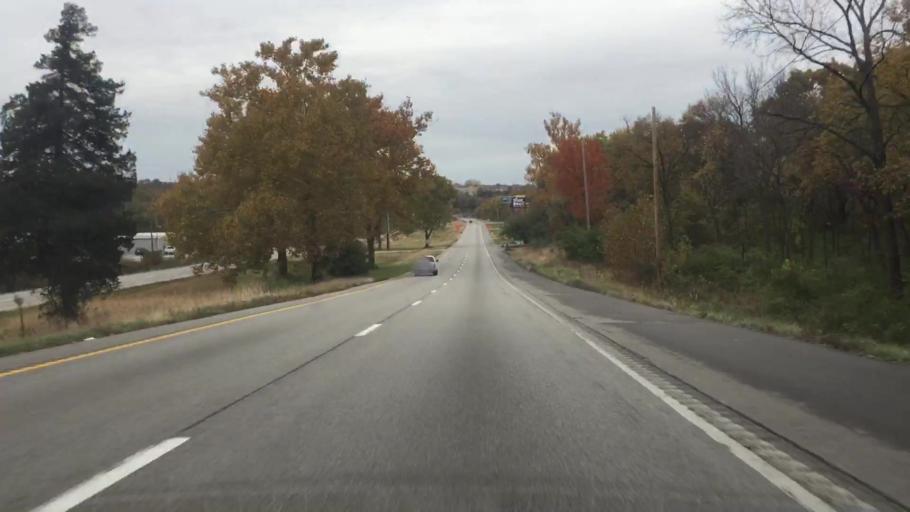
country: US
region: Missouri
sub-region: Jackson County
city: Lees Summit
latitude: 38.9586
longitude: -94.4220
